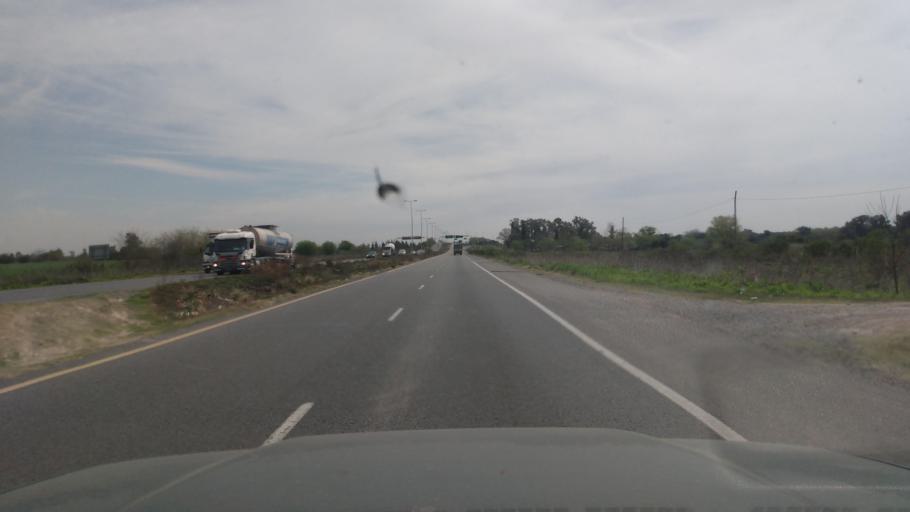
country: AR
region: Buenos Aires
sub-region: Partido de Lujan
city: Lujan
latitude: -34.4767
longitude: -59.0643
